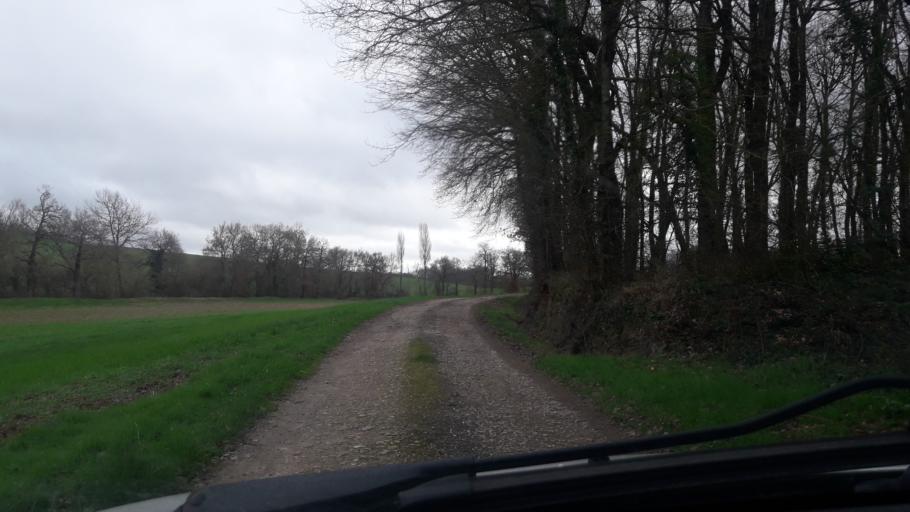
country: FR
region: Midi-Pyrenees
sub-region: Departement du Gers
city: Gimont
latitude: 43.6554
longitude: 0.9761
